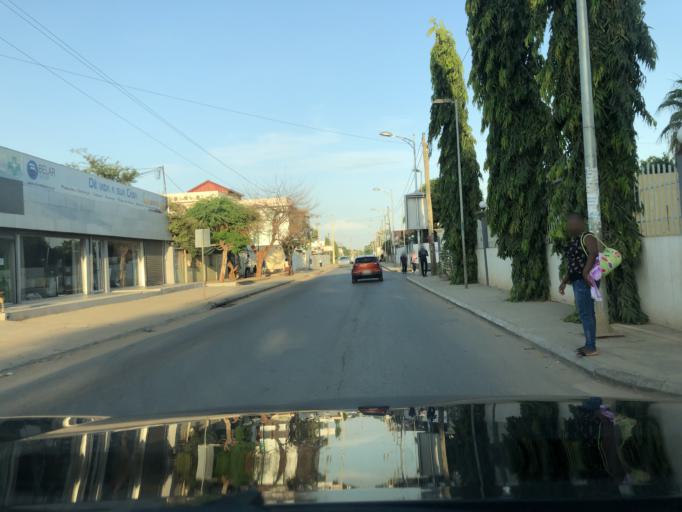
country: AO
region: Luanda
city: Luanda
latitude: -8.9476
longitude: 13.1655
